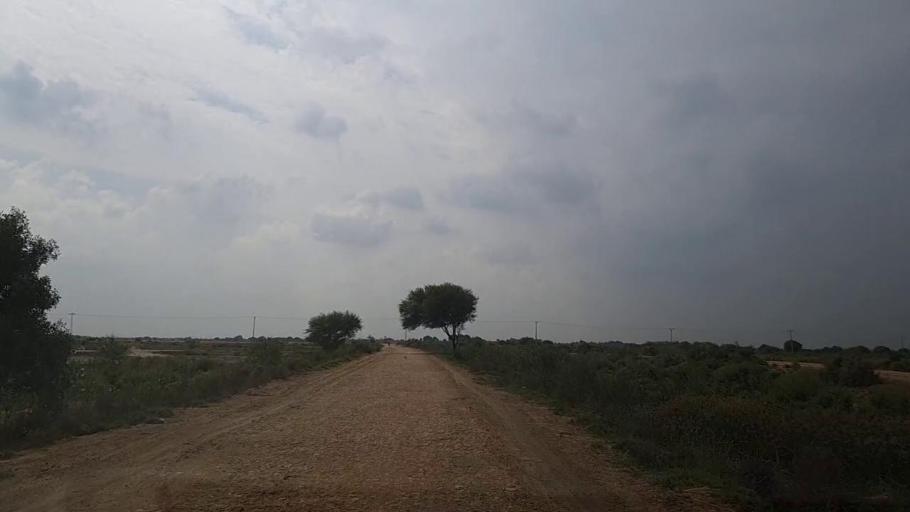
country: PK
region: Sindh
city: Mirpur Batoro
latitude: 24.5853
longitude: 68.1209
